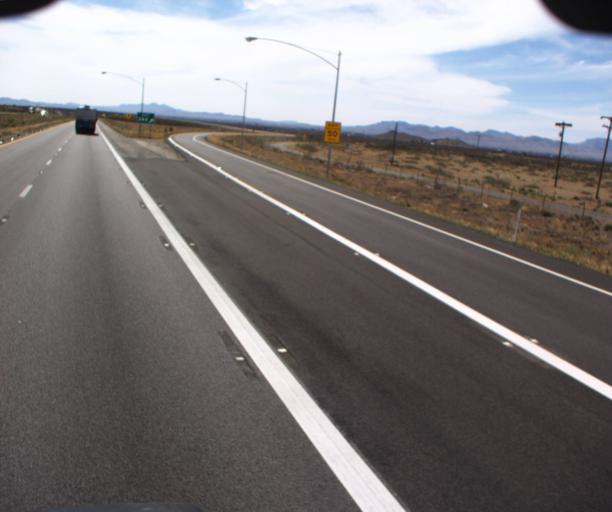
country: US
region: Arizona
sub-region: Cochise County
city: Willcox
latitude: 32.3123
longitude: -109.7911
